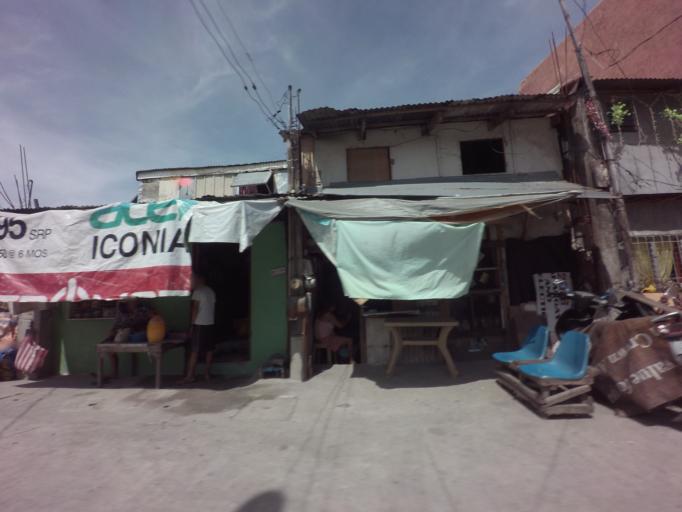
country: PH
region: Calabarzon
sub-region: Province of Rizal
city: Pateros
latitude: 14.5333
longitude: 121.0748
